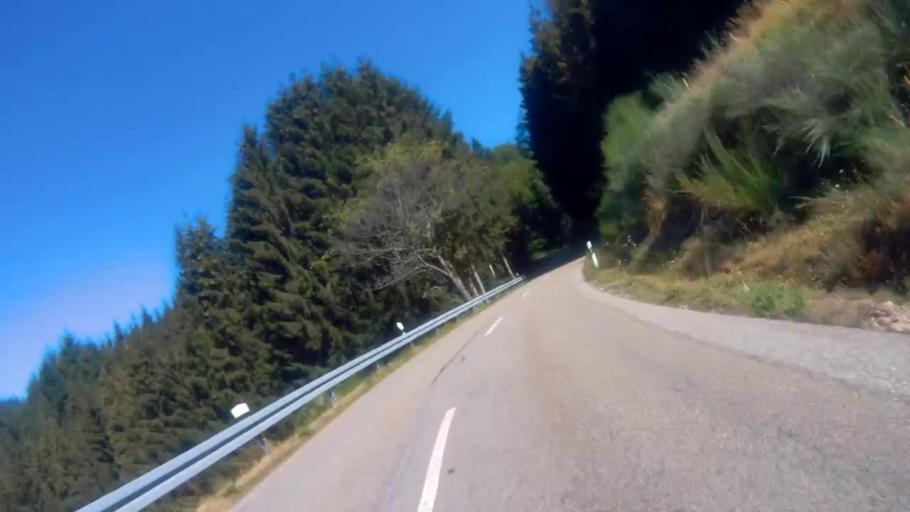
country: DE
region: Baden-Wuerttemberg
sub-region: Freiburg Region
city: Bollen
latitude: 47.7560
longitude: 7.7595
